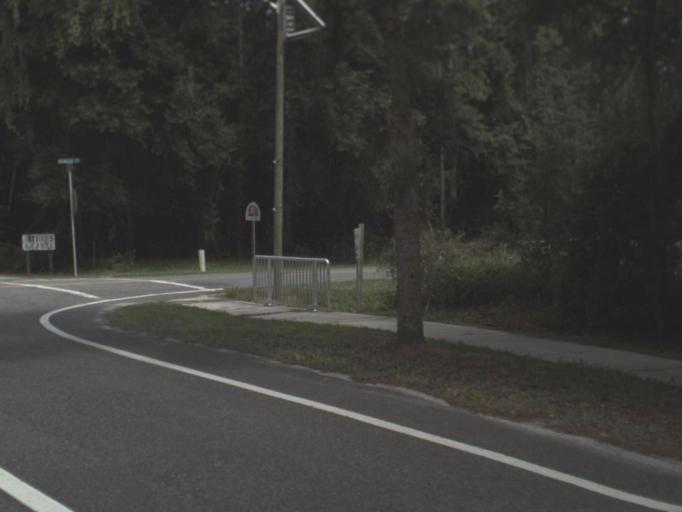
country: US
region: Florida
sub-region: Clay County
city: Asbury Lake
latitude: 29.9824
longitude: -81.8203
